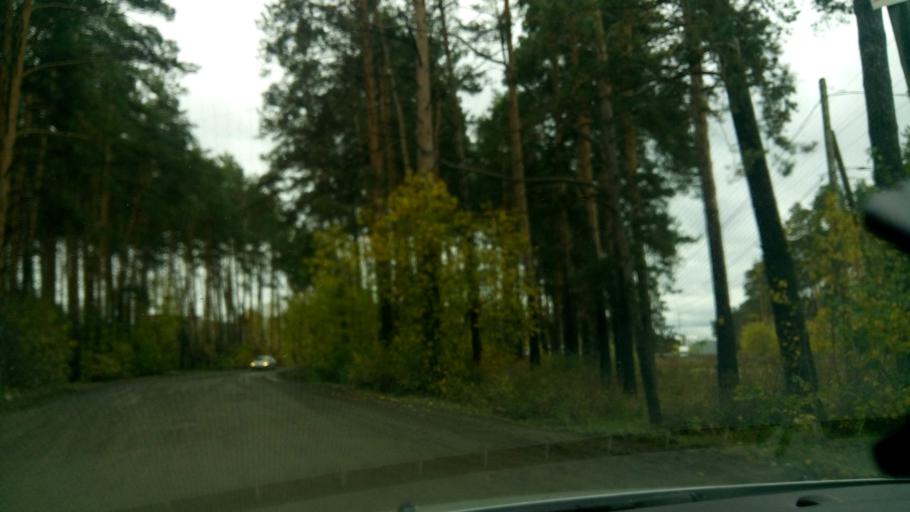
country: RU
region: Sverdlovsk
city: Shirokaya Rechka
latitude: 56.8180
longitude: 60.5231
